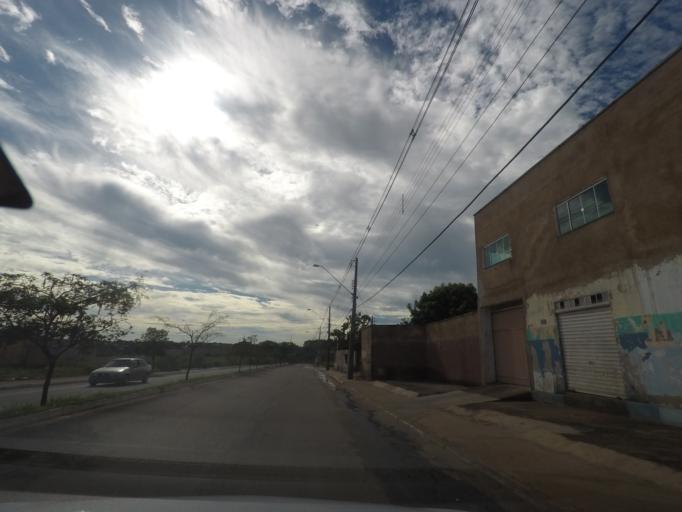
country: BR
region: Goias
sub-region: Aparecida De Goiania
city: Aparecida de Goiania
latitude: -16.8170
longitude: -49.3088
